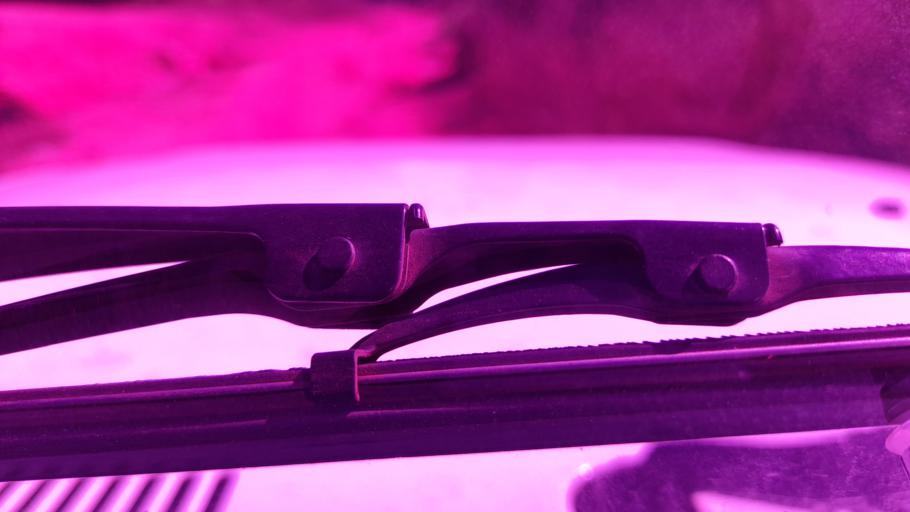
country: SN
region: Ziguinchor
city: Adeane
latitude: 12.4101
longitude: -15.7816
